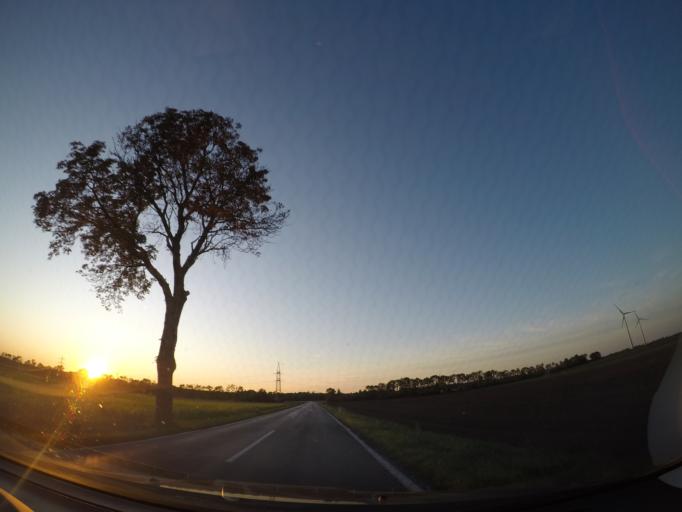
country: AT
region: Lower Austria
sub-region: Politischer Bezirk Bruck an der Leitha
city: Au am Leithaberge
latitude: 47.9498
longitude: 16.5482
